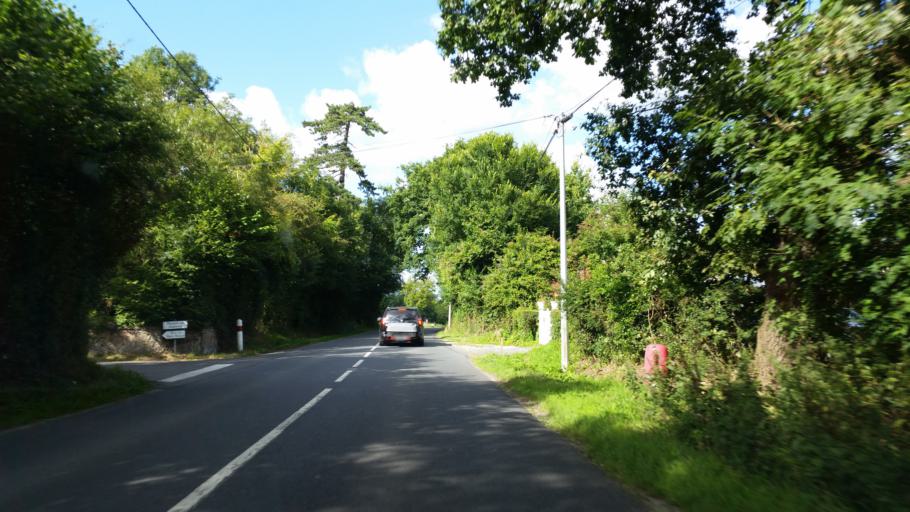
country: FR
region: Lower Normandy
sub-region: Departement du Calvados
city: Blonville-sur-Mer
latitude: 49.3117
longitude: 0.0458
